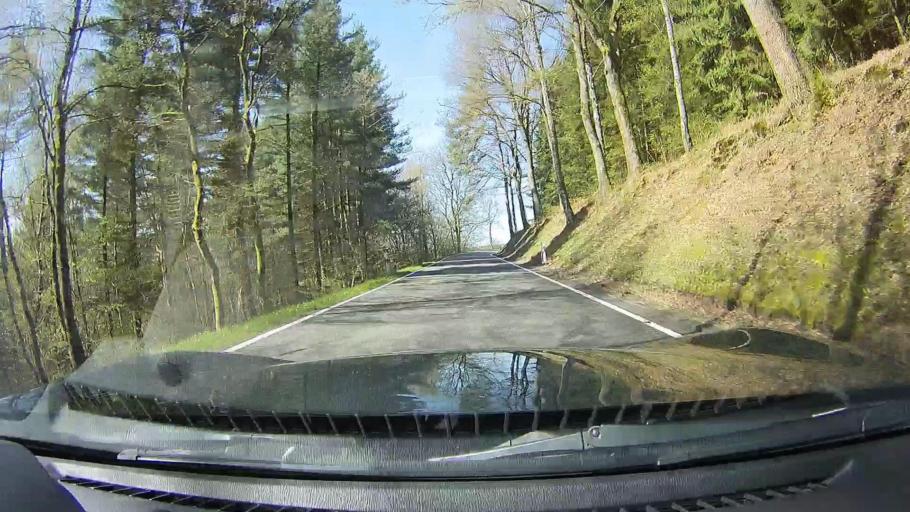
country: DE
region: Hesse
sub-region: Regierungsbezirk Darmstadt
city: Rothenberg
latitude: 49.4919
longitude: 8.9191
